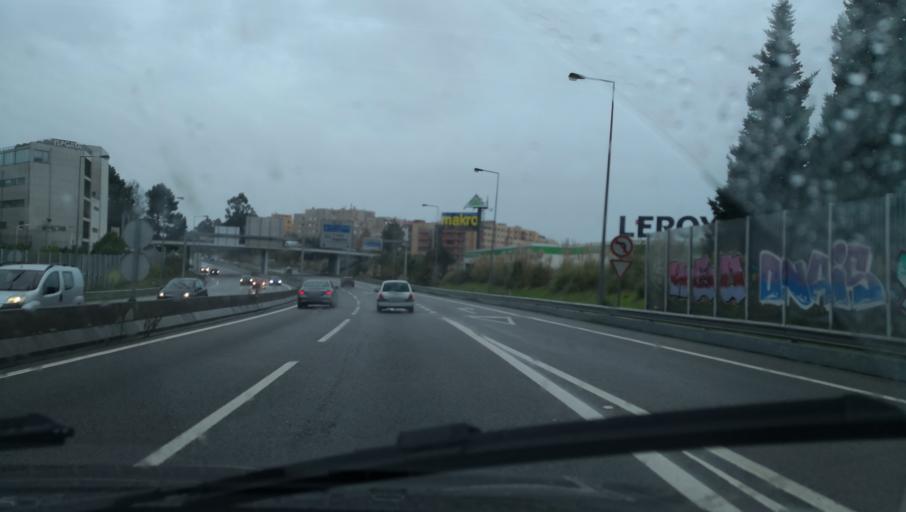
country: PT
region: Porto
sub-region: Vila Nova de Gaia
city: Vila Nova de Gaia
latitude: 41.1211
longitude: -8.6227
